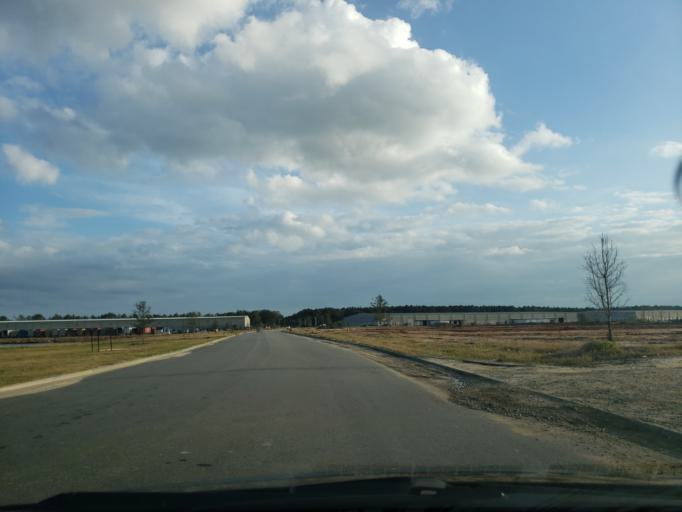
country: US
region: Georgia
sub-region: Chatham County
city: Bloomingdale
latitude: 32.1650
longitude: -81.2700
